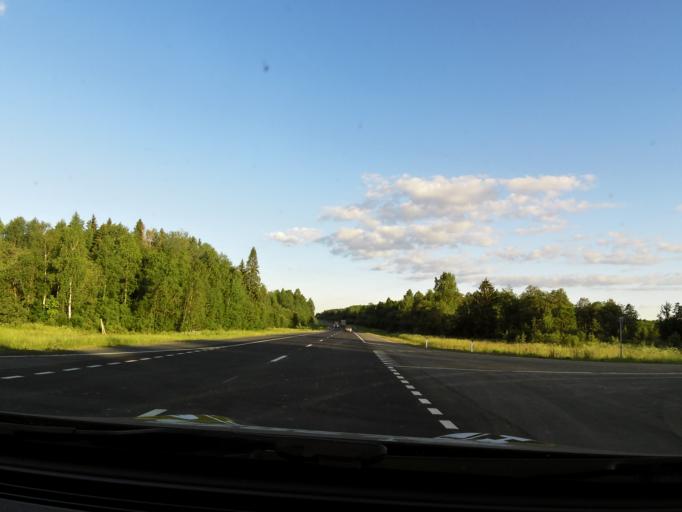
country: RU
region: Vologda
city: Gryazovets
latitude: 59.0093
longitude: 40.1219
